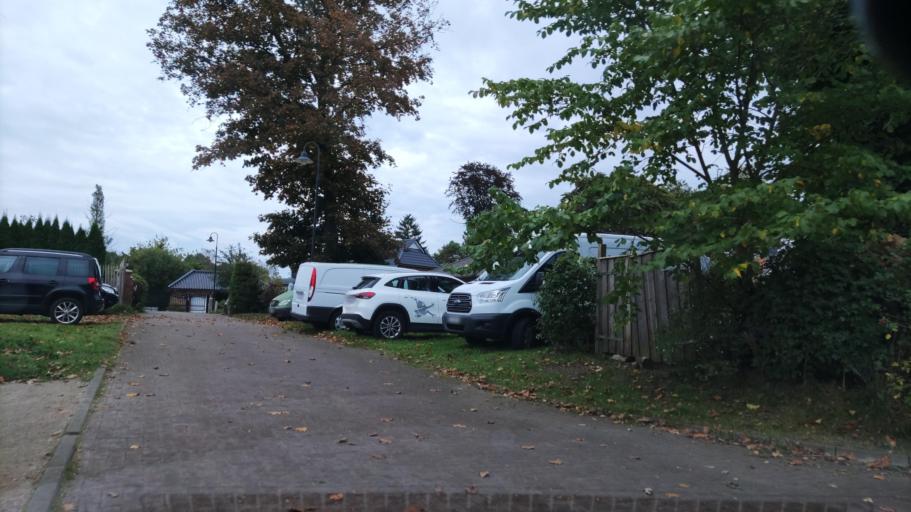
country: DE
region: Schleswig-Holstein
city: Trittau
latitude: 53.6082
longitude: 10.4133
